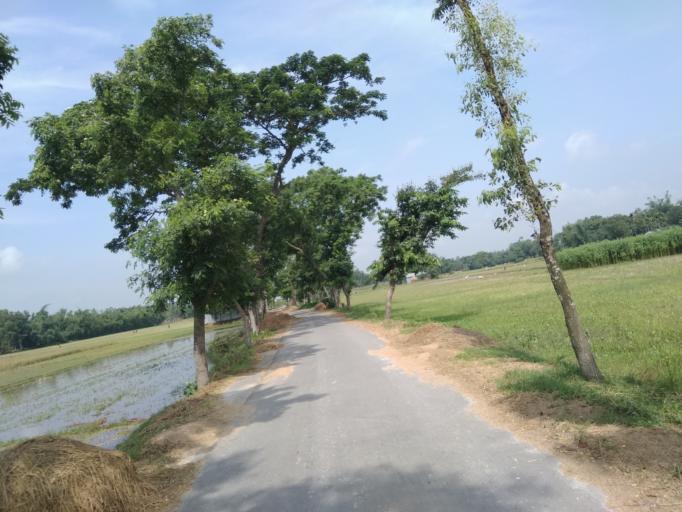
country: BD
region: Rangpur Division
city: Rangpur
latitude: 25.8369
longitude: 89.2028
